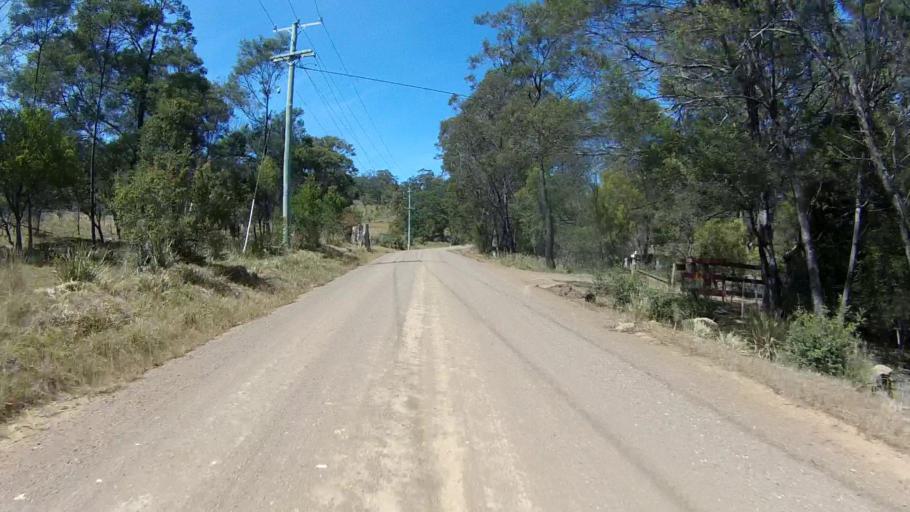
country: AU
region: Tasmania
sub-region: Sorell
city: Sorell
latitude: -42.7679
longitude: 147.6524
